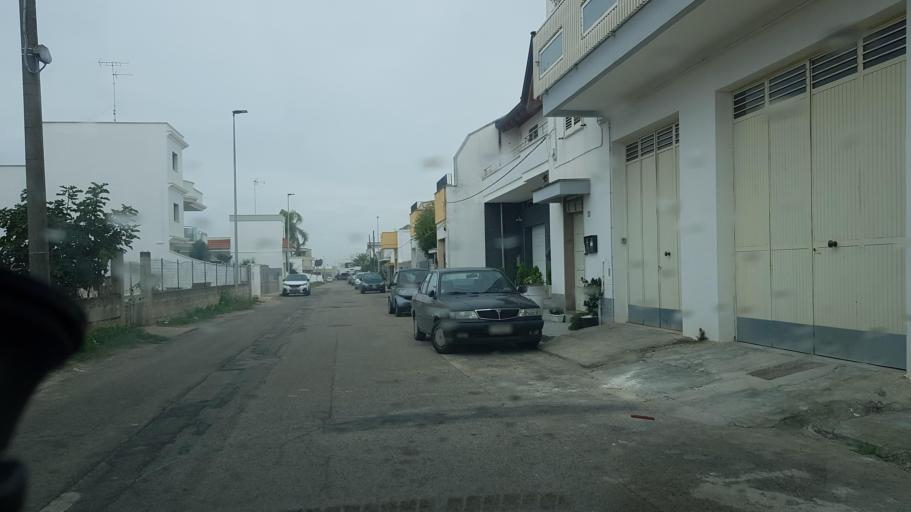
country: IT
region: Apulia
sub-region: Provincia di Lecce
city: Leverano
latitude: 40.2825
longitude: 17.9919
